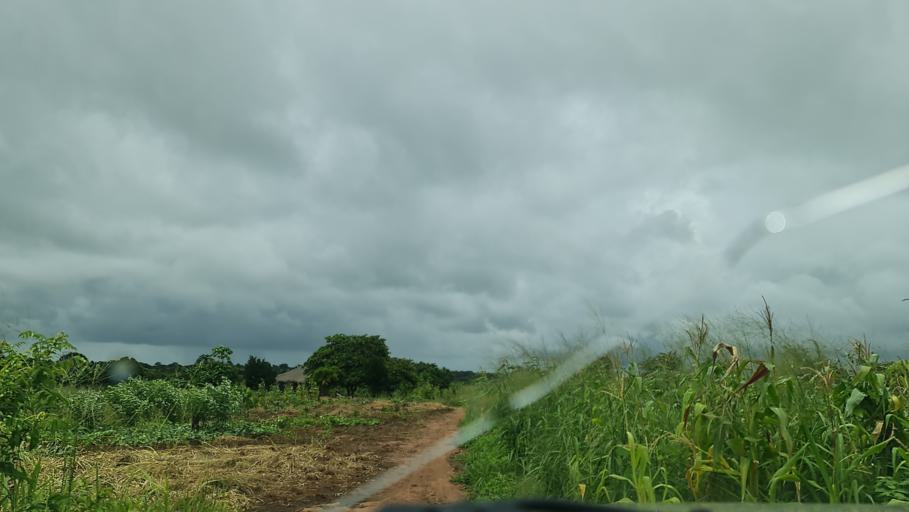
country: MW
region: Southern Region
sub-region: Nsanje District
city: Nsanje
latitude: -17.3928
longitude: 35.7837
